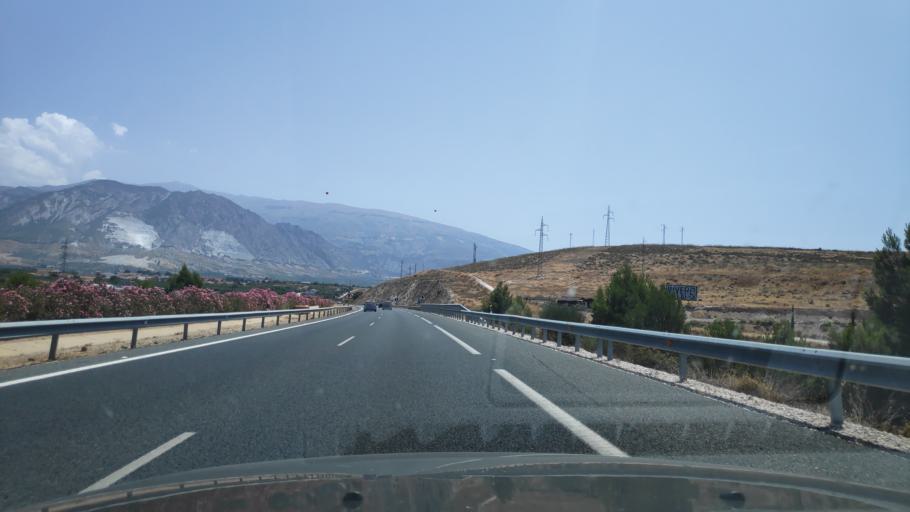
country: ES
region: Andalusia
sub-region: Provincia de Granada
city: Durcal
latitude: 36.9880
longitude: -3.6060
